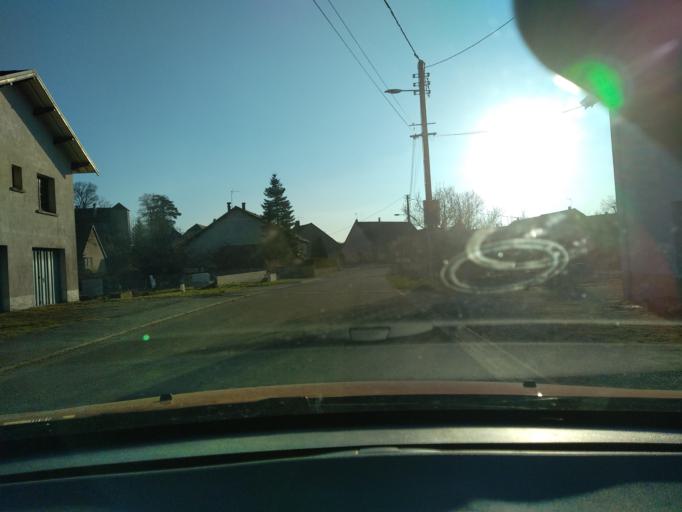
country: FR
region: Franche-Comte
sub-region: Departement du Jura
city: Perrigny
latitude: 46.6349
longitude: 5.6423
